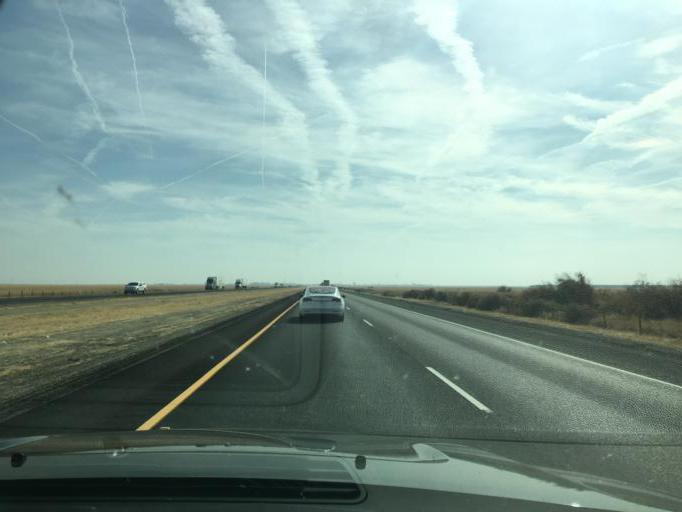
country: US
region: California
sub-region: Kern County
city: Lost Hills
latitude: 35.6469
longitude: -119.6762
